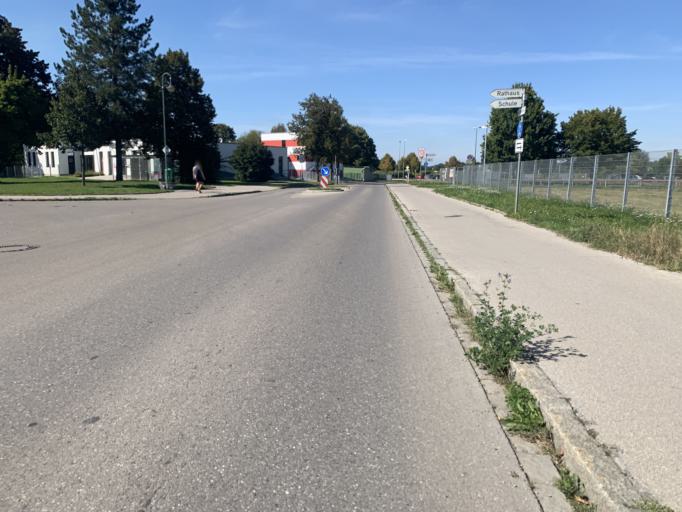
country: DE
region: Bavaria
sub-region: Swabia
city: Kissing
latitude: 48.3041
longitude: 10.9810
